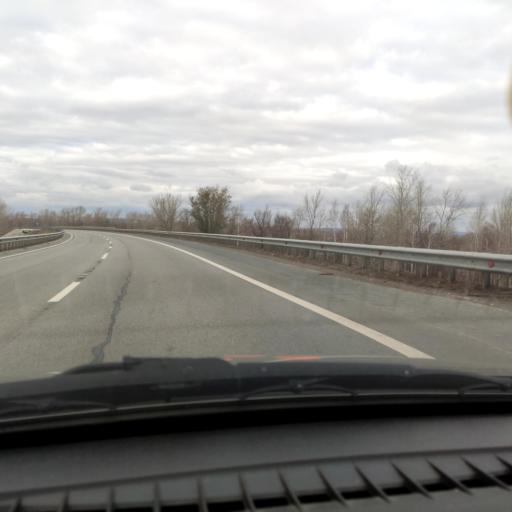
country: RU
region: Samara
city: Novosemeykino
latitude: 53.4148
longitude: 50.3398
